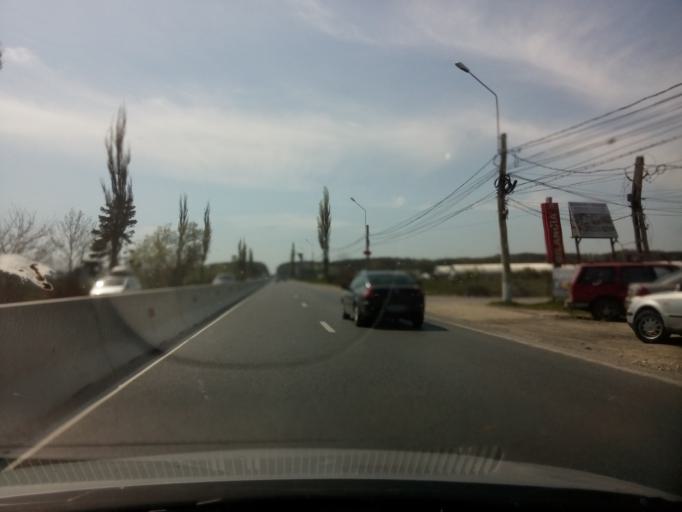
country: RO
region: Ilfov
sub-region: Comuna Corbeanca
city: Corbeanca
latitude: 44.5965
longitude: 26.0712
